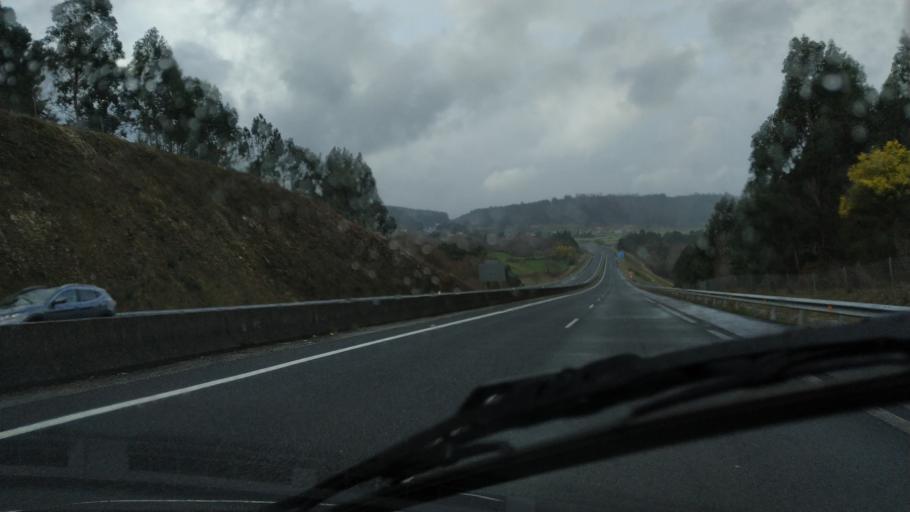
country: ES
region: Galicia
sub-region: Provincia de Pontevedra
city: Silleda
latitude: 42.7239
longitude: -8.3173
